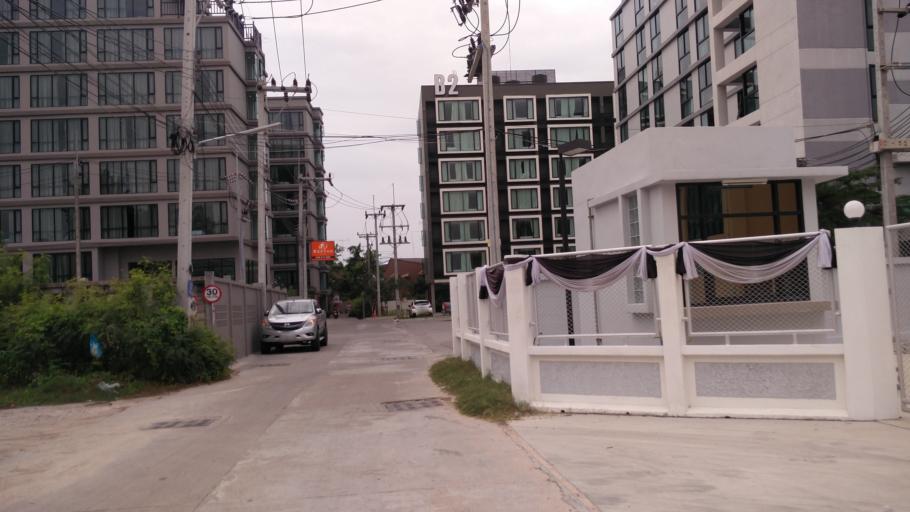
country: TH
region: Chon Buri
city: Phatthaya
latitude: 12.9219
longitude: 100.8839
